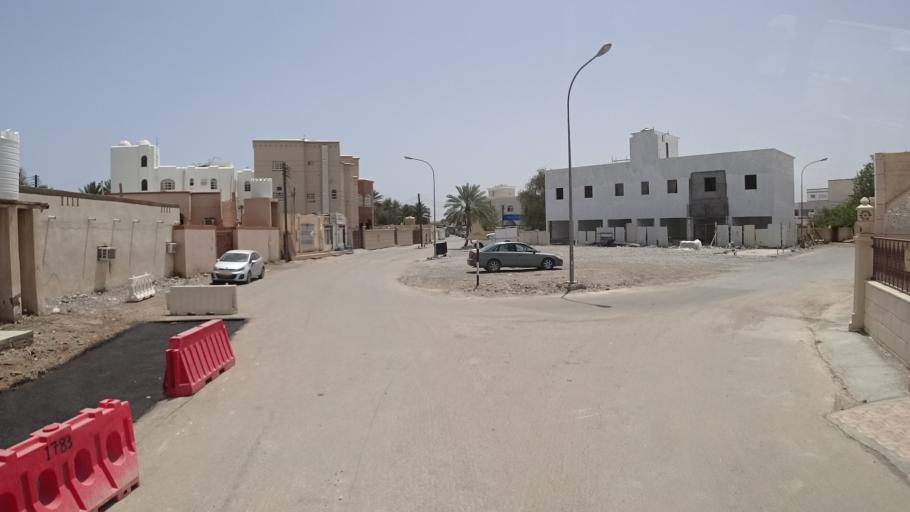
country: OM
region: Muhafazat Masqat
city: Muscat
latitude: 23.2611
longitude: 58.9144
